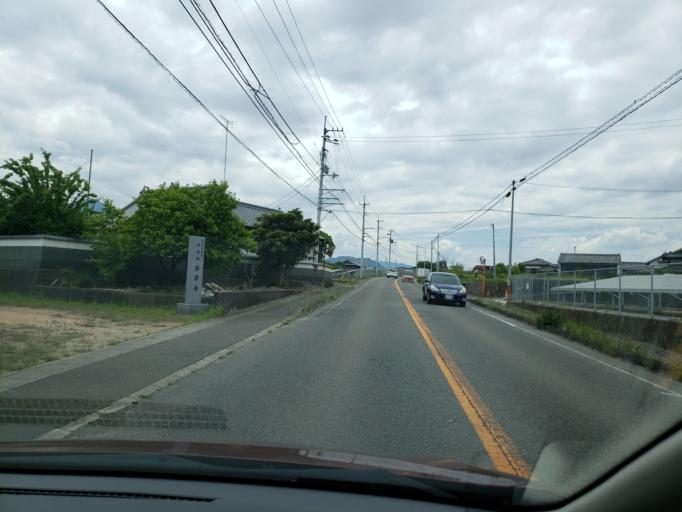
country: JP
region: Tokushima
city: Kamojimacho-jogejima
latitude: 34.0794
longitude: 134.2540
